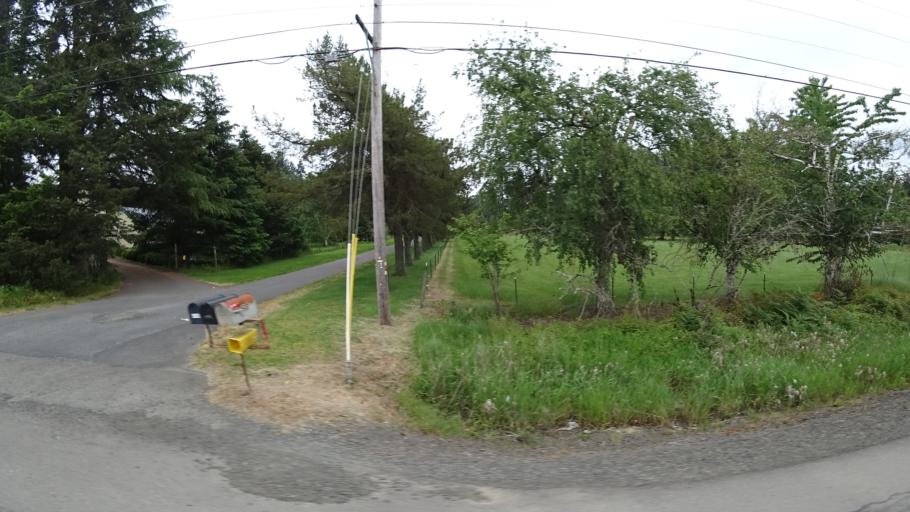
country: US
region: Oregon
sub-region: Washington County
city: Hillsboro
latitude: 45.4896
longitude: -122.9910
